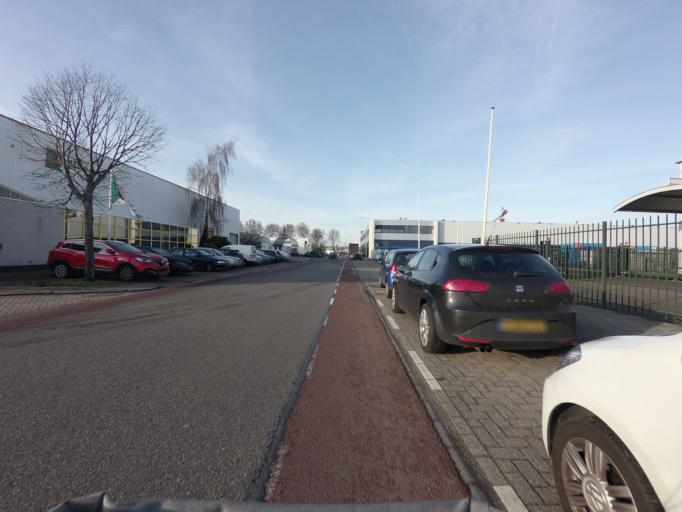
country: NL
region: Utrecht
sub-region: Stichtse Vecht
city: Maarssen
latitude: 52.1224
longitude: 5.0523
